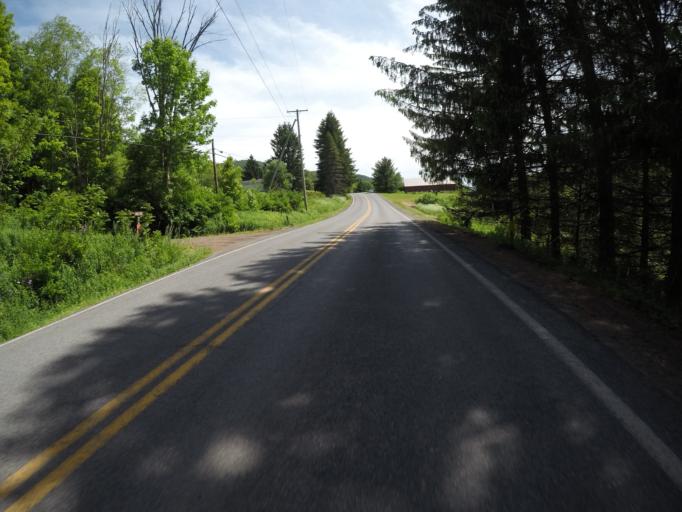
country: US
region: New York
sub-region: Delaware County
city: Delhi
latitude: 42.1504
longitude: -74.7980
